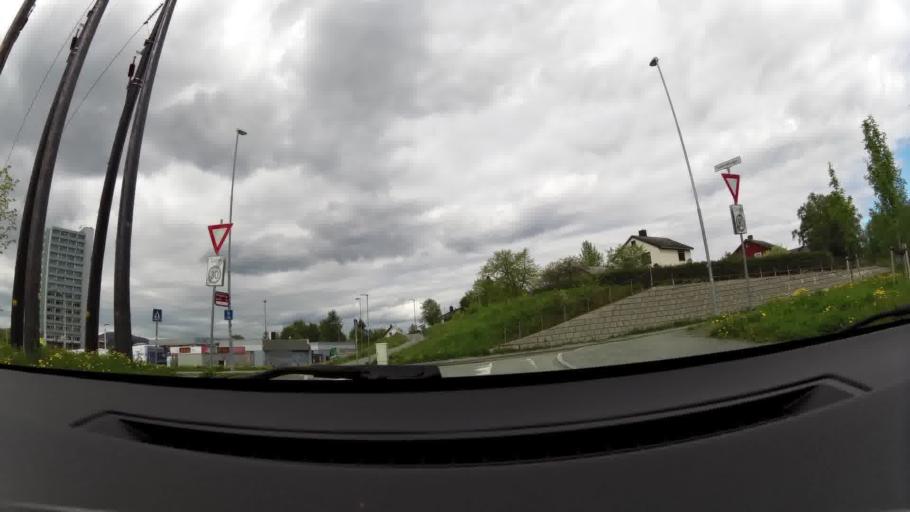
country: NO
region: Sor-Trondelag
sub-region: Trondheim
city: Trondheim
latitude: 63.3908
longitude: 10.4340
